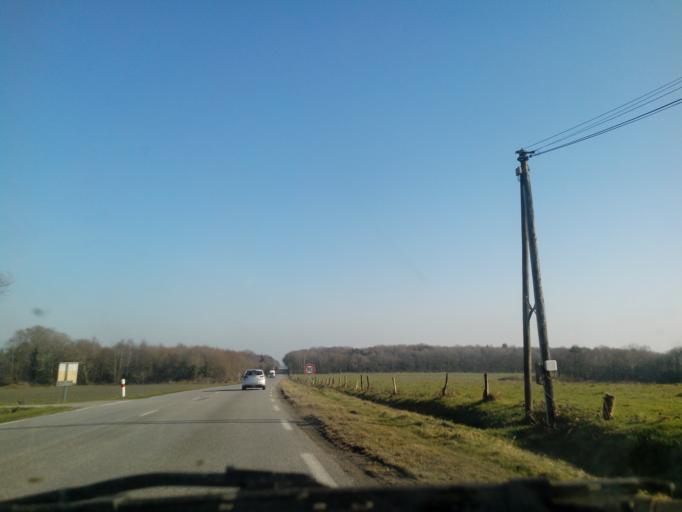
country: FR
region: Brittany
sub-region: Departement du Morbihan
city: Meneac
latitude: 48.1986
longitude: -2.4781
